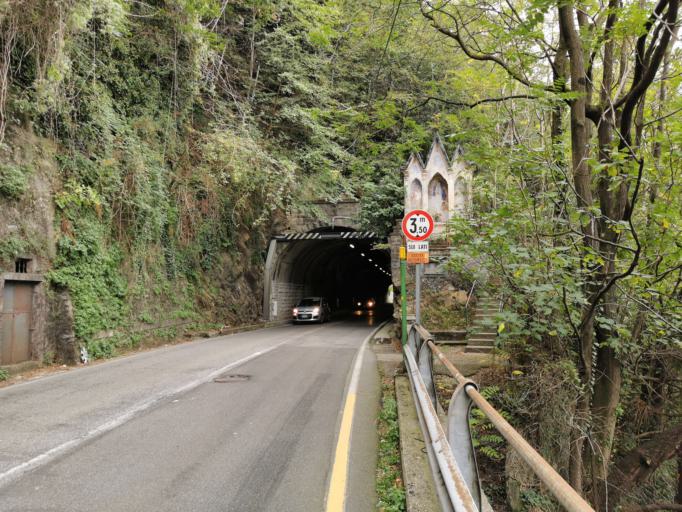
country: IT
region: Lombardy
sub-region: Provincia di Lecco
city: Bellano
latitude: 46.0329
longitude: 9.2961
